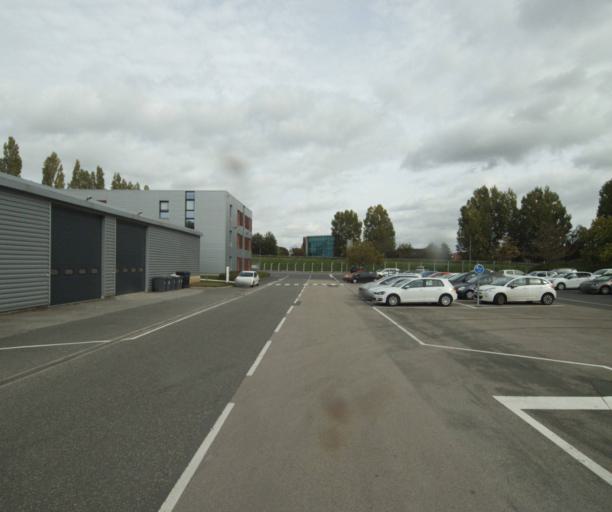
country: FR
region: Nord-Pas-de-Calais
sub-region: Departement du Nord
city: Erquinghem-Lys
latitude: 50.6763
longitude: 2.8333
